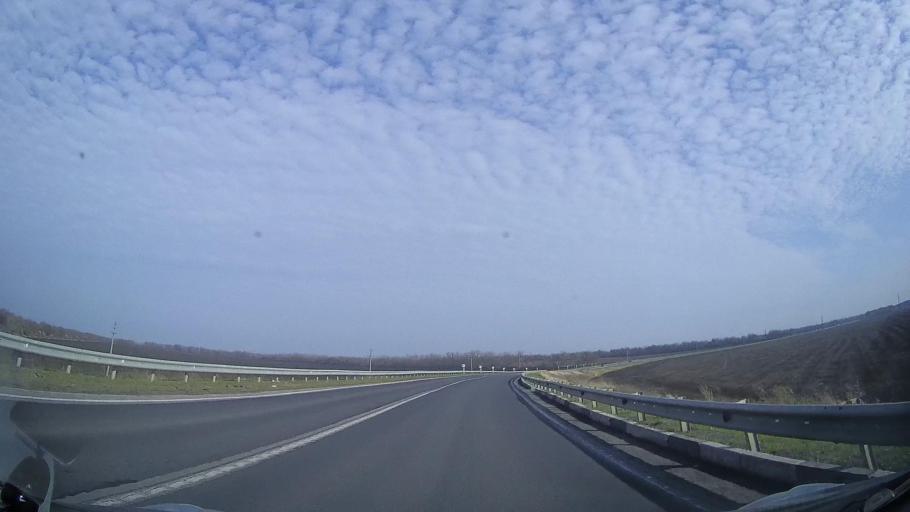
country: RU
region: Rostov
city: Tselina
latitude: 46.5301
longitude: 41.1693
